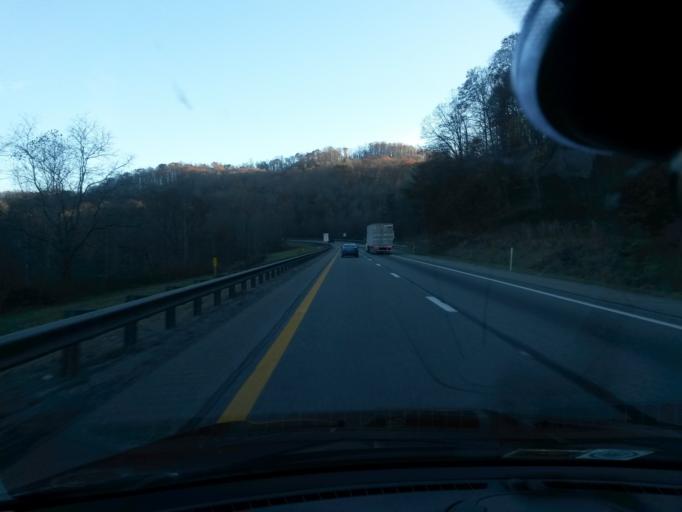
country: US
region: West Virginia
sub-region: Raleigh County
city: Prosperity
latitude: 37.8531
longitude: -81.2531
